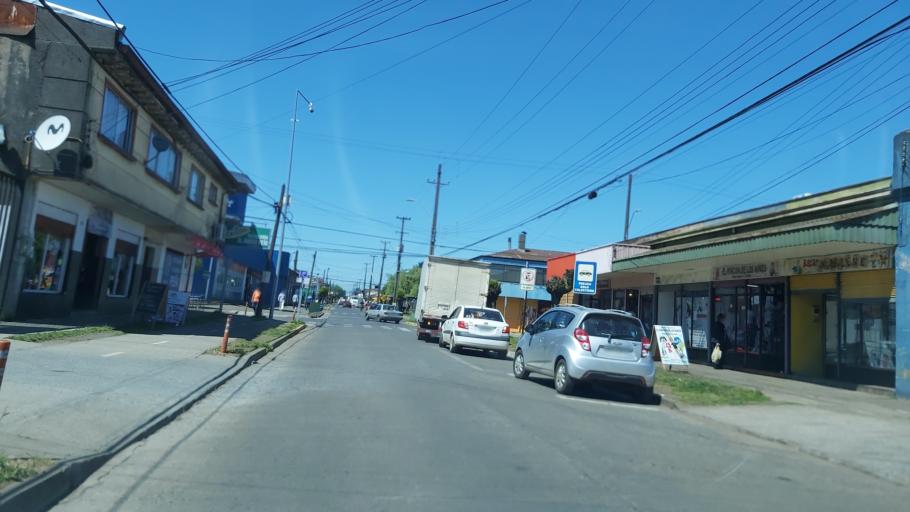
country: CL
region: Araucania
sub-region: Provincia de Malleco
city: Victoria
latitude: -38.2341
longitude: -72.3294
